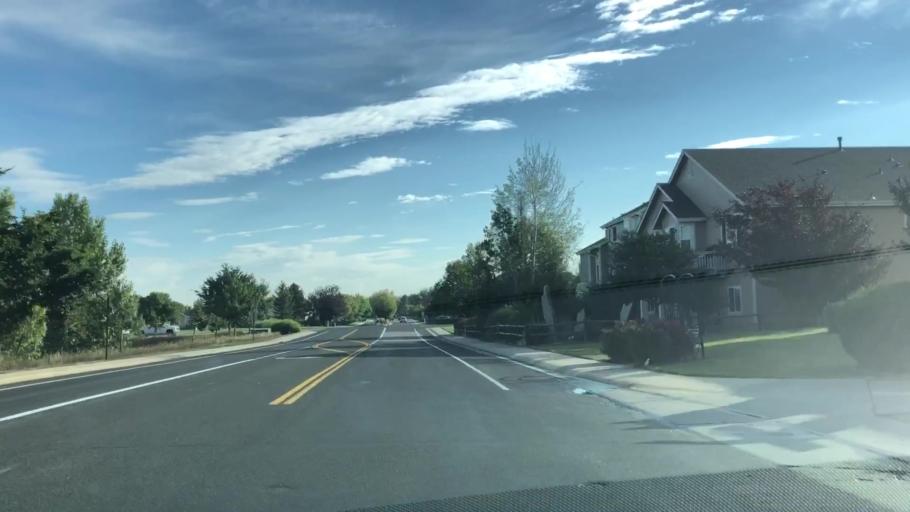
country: US
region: Colorado
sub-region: Weld County
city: Windsor
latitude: 40.4743
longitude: -104.9780
